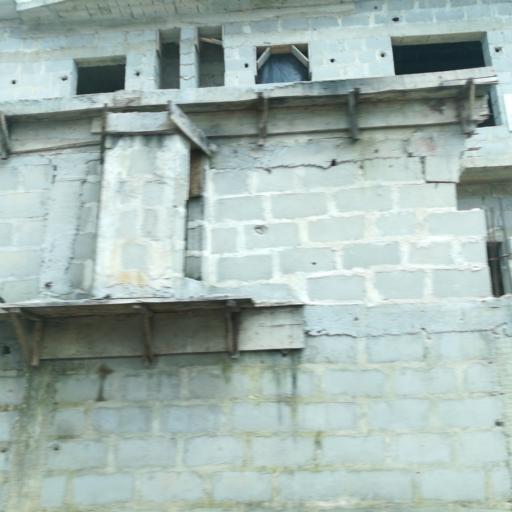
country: NG
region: Rivers
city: Port Harcourt
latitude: 4.8101
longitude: 7.0648
